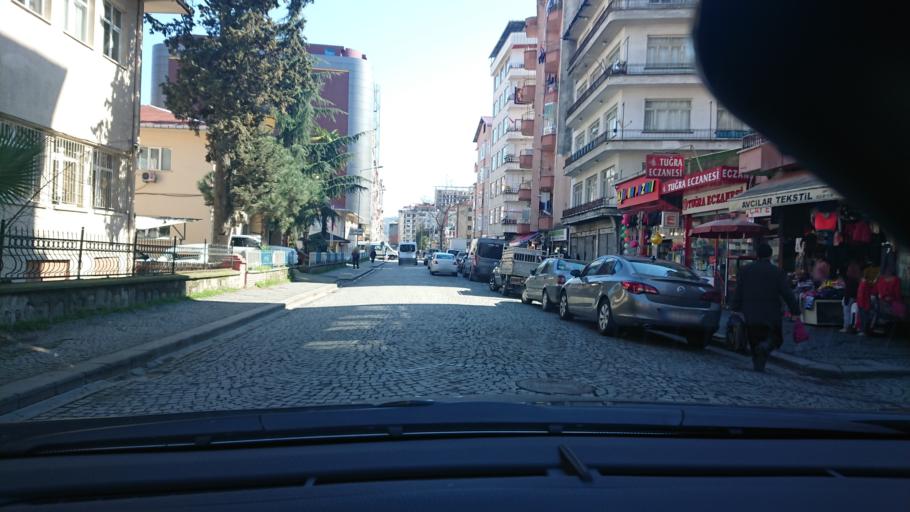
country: TR
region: Rize
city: Rize
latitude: 41.0231
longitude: 40.5271
